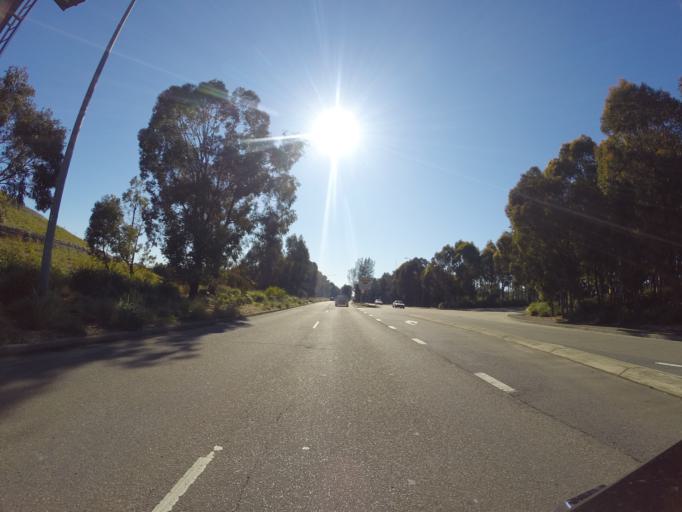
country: AU
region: New South Wales
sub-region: Auburn
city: Auburn
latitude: -33.8458
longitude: 151.0566
